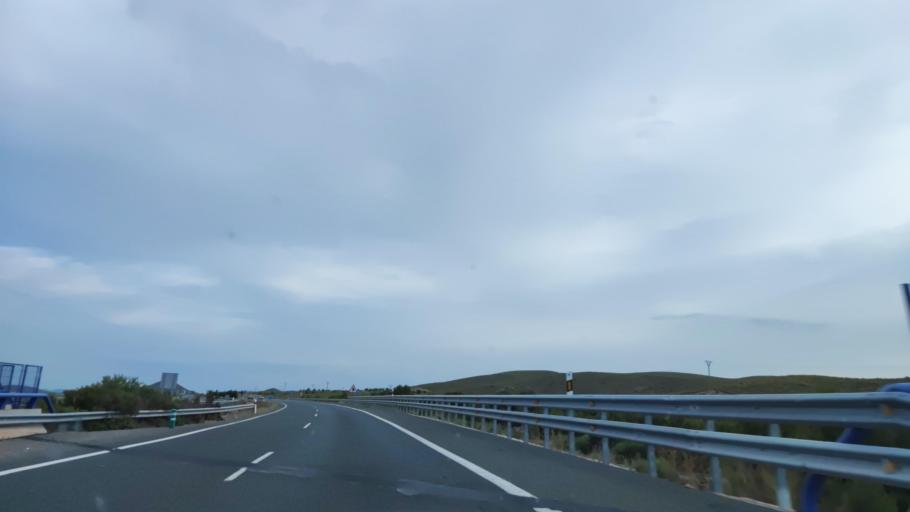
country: ES
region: Castille-La Mancha
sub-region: Provincia de Albacete
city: Tobarra
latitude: 38.5756
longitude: -1.6869
